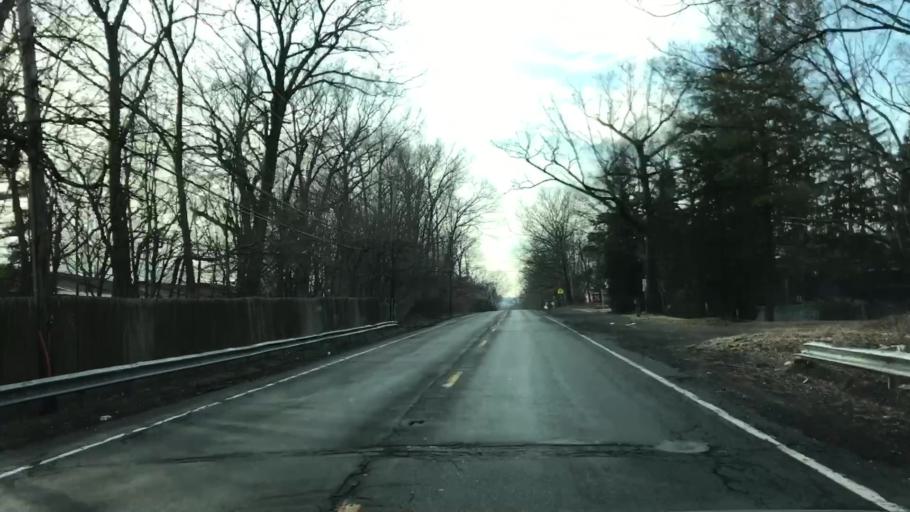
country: US
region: New York
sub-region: Rockland County
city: Congers
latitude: 41.1558
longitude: -73.9349
